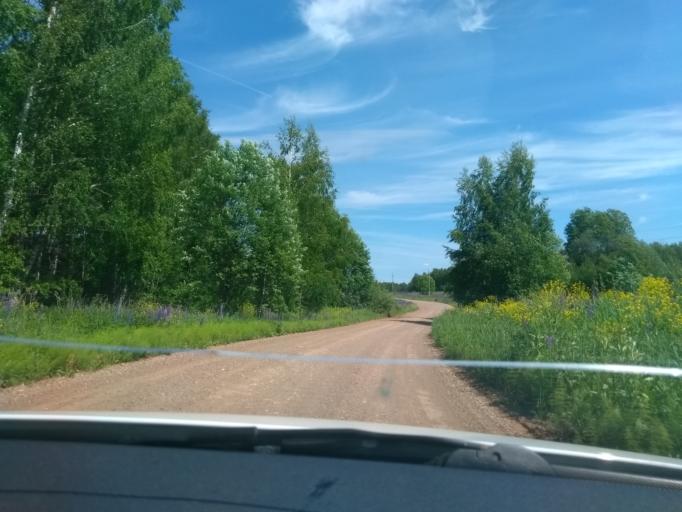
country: RU
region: Perm
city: Sylva
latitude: 57.8174
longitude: 56.7311
